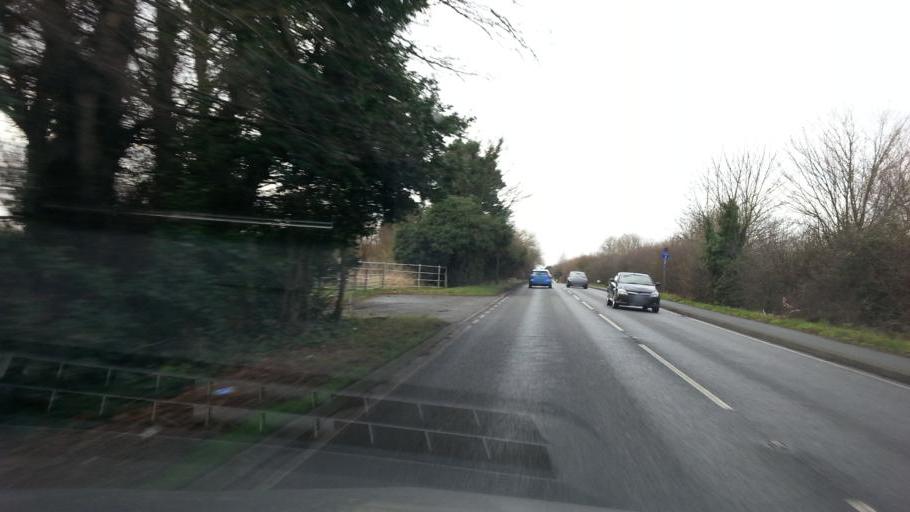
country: GB
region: England
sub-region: Leicestershire
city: Castle Donington
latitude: 52.8675
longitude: -1.3135
